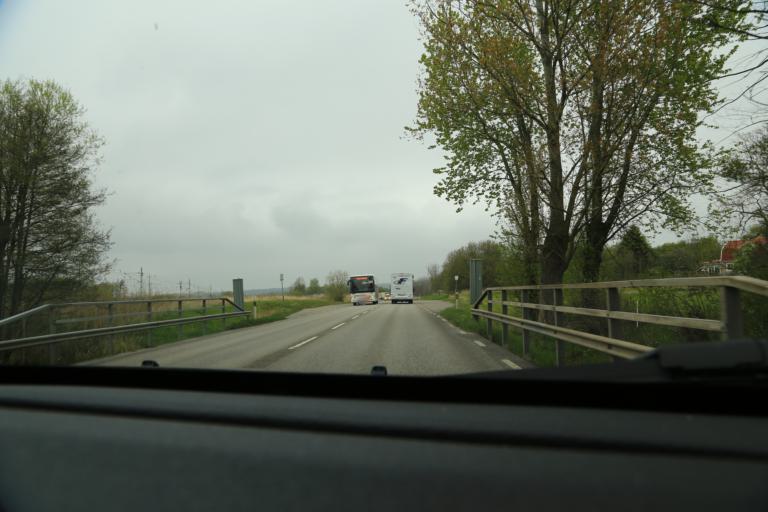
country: SE
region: Halland
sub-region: Varbergs Kommun
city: Veddige
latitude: 57.2120
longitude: 12.2219
